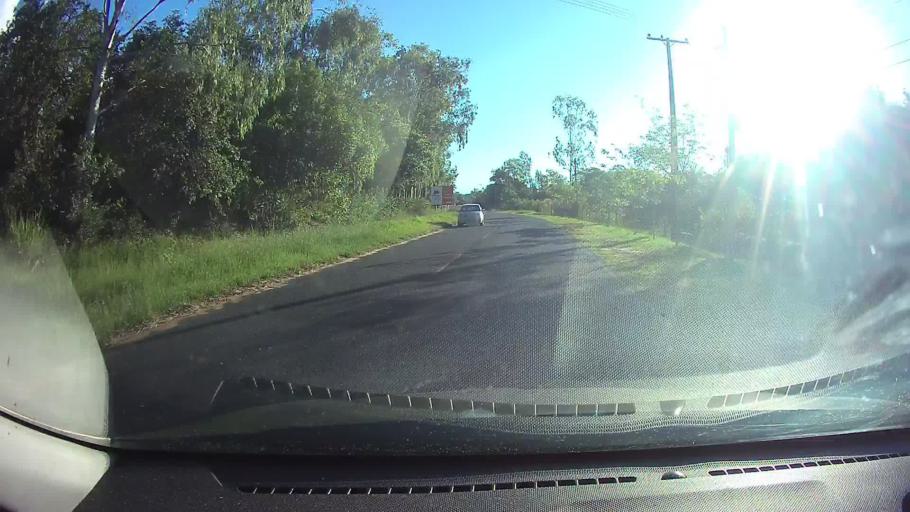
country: PY
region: Cordillera
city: Emboscada
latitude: -25.1818
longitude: -57.2951
